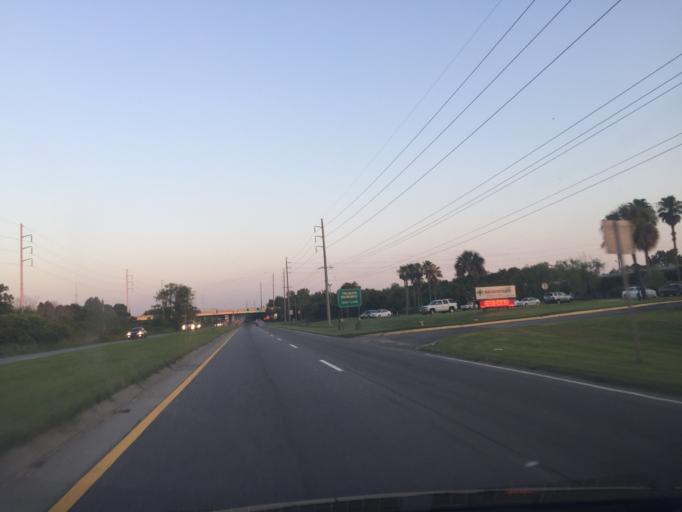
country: US
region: Georgia
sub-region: Chatham County
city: Savannah
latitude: 32.0725
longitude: -81.0689
